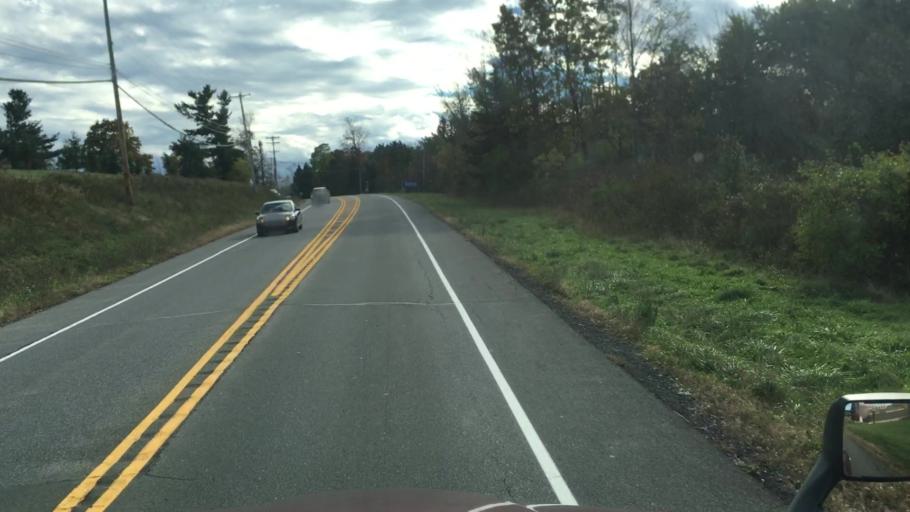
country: US
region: New York
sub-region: Saratoga County
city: Ballston Spa
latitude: 42.9697
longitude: -73.8633
